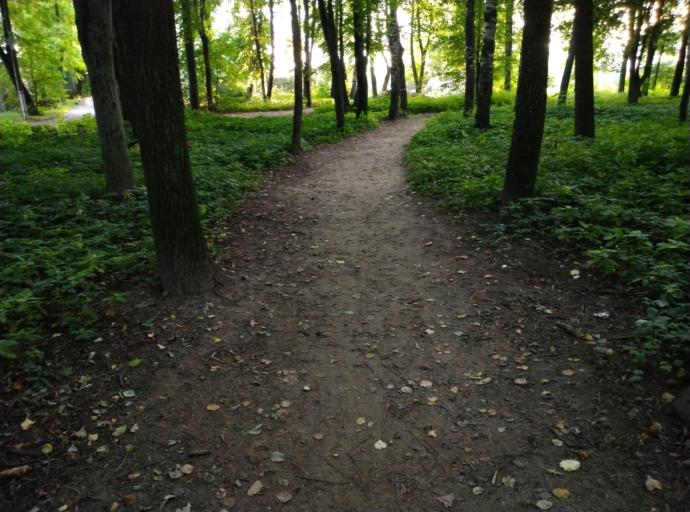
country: RU
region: Kostroma
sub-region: Kostromskoy Rayon
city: Kostroma
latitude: 57.7526
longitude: 40.9583
